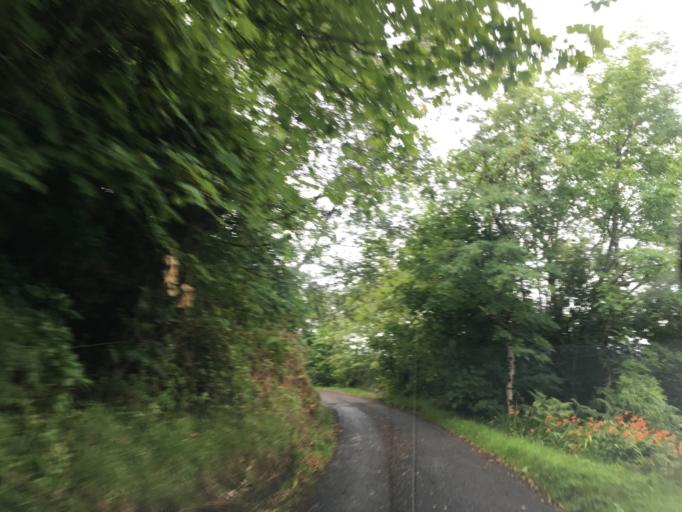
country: GB
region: Scotland
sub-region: Argyll and Bute
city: Oban
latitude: 56.2607
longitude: -5.4715
